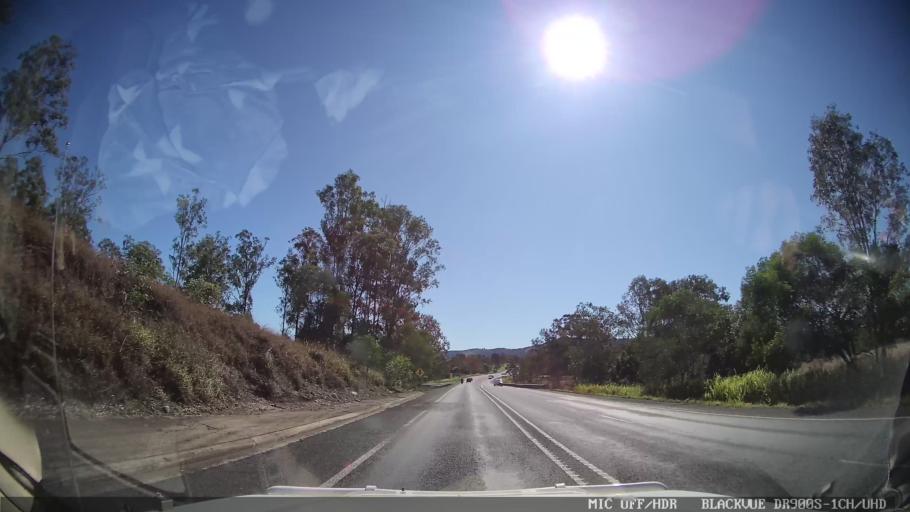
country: AU
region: Queensland
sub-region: Gympie Regional Council
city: Gympie
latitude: -25.9987
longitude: 152.5663
